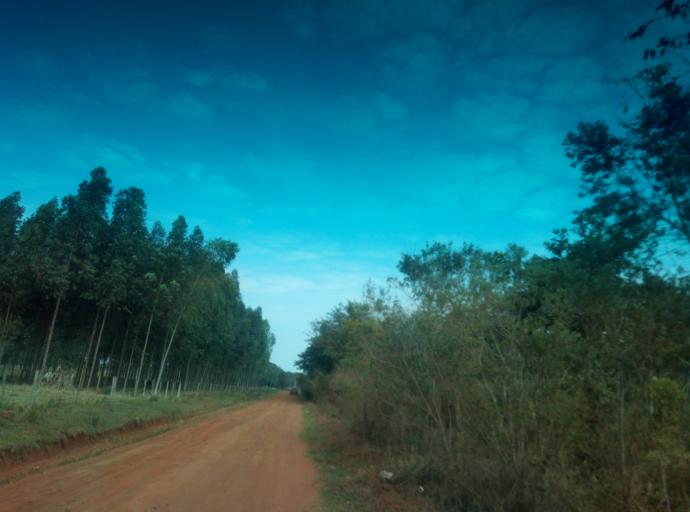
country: PY
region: Caaguazu
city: Carayao
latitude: -25.1940
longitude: -56.2520
